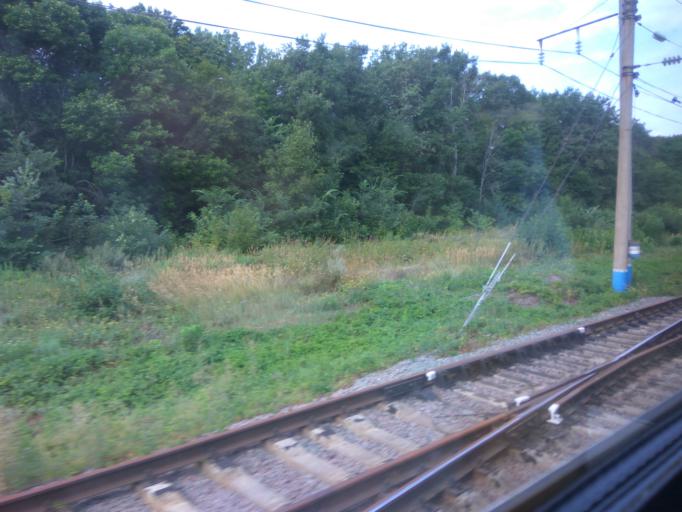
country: RU
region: Saratov
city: Rtishchevo
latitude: 52.2042
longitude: 43.8919
